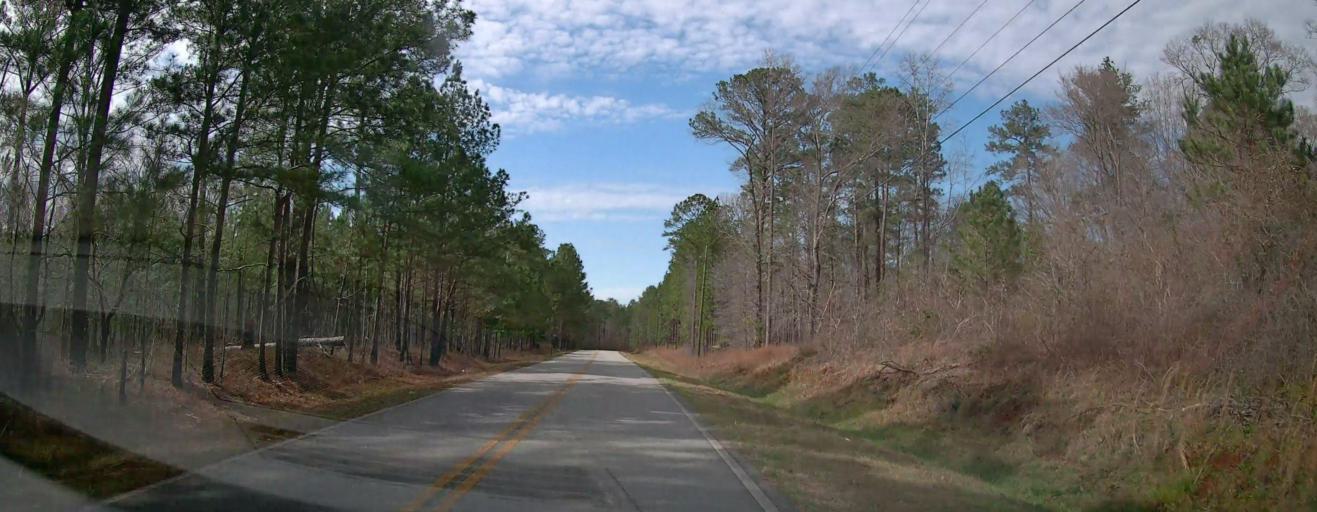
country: US
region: Georgia
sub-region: Jones County
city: Gray
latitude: 33.0317
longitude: -83.7057
